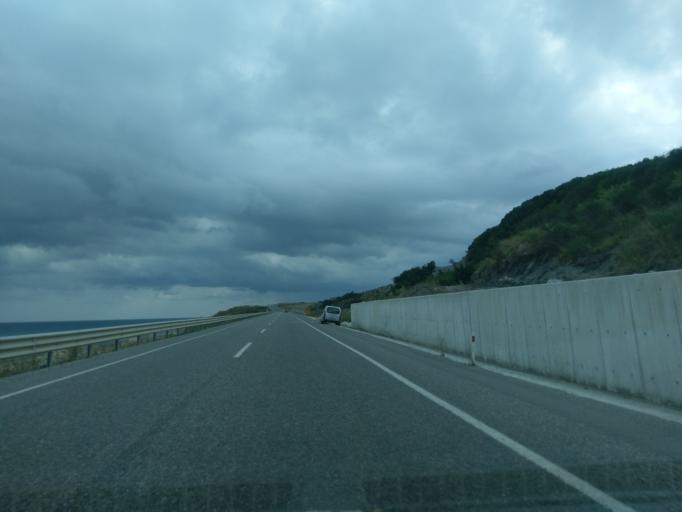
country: TR
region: Sinop
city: Helaldi
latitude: 41.9492
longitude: 34.3718
